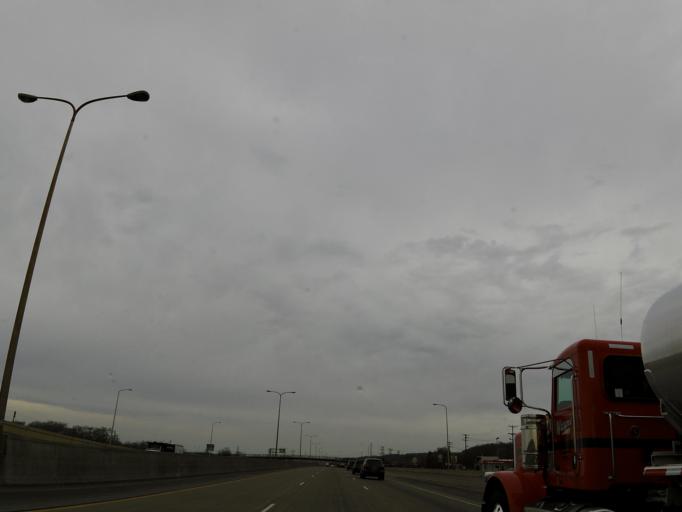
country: US
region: Minnesota
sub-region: Washington County
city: Newport
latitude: 44.8734
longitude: -93.0006
